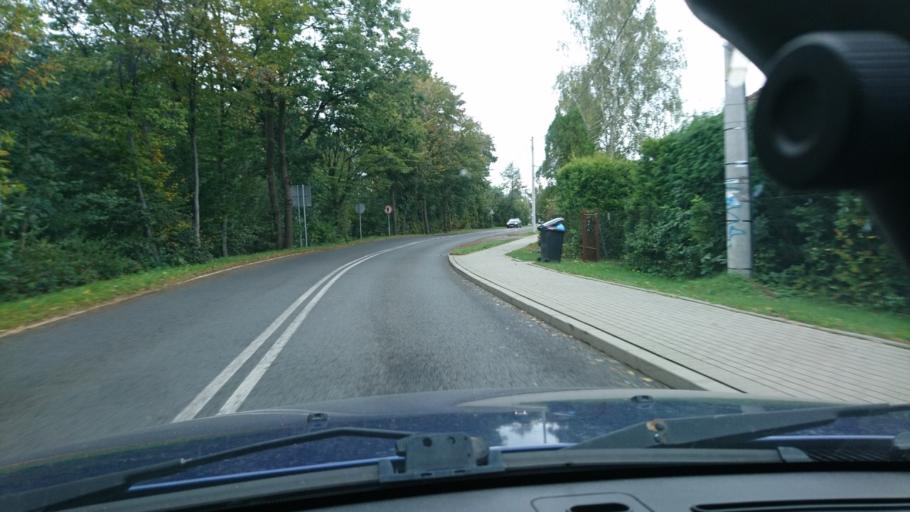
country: PL
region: Silesian Voivodeship
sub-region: Powiat bielski
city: Jaworze
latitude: 49.8000
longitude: 18.9843
